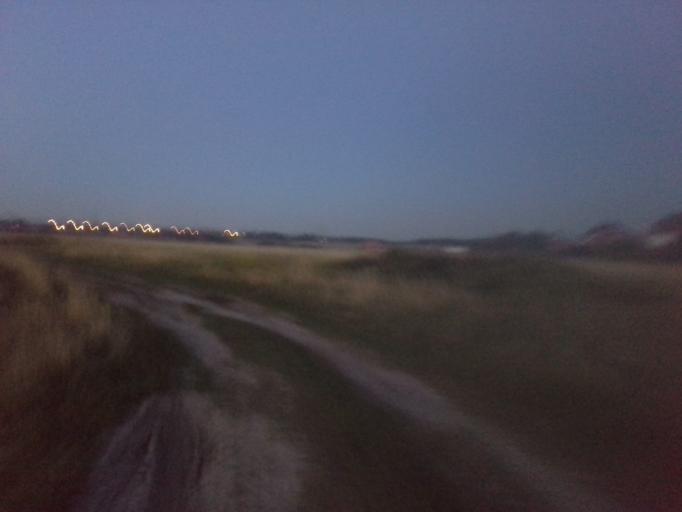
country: RU
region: Moskovskaya
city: Zhavoronki
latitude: 55.6514
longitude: 37.1205
